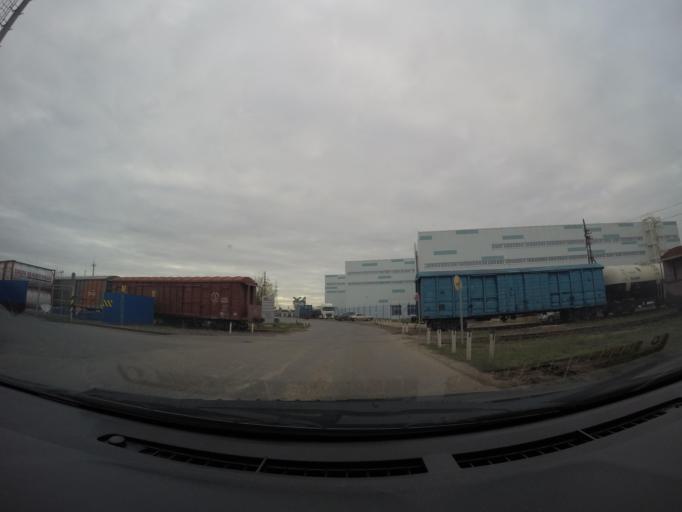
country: RU
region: Moskovskaya
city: Staraya Kupavna
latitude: 55.7909
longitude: 38.1840
